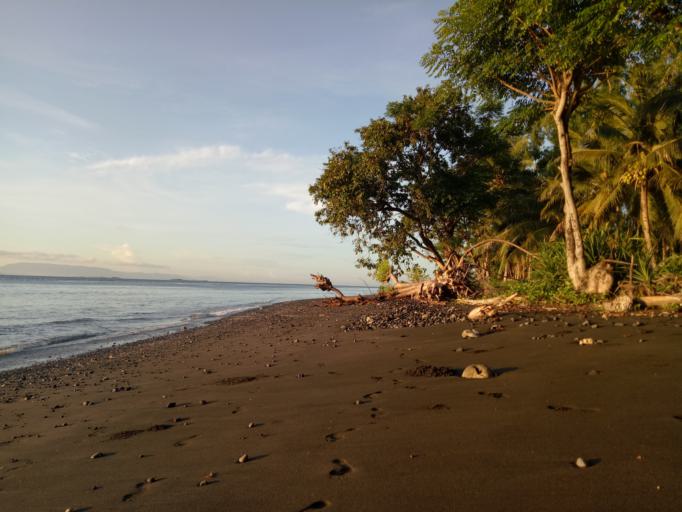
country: ID
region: West Nusa Tenggara
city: Sambelia
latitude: -8.3961
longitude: 116.7225
